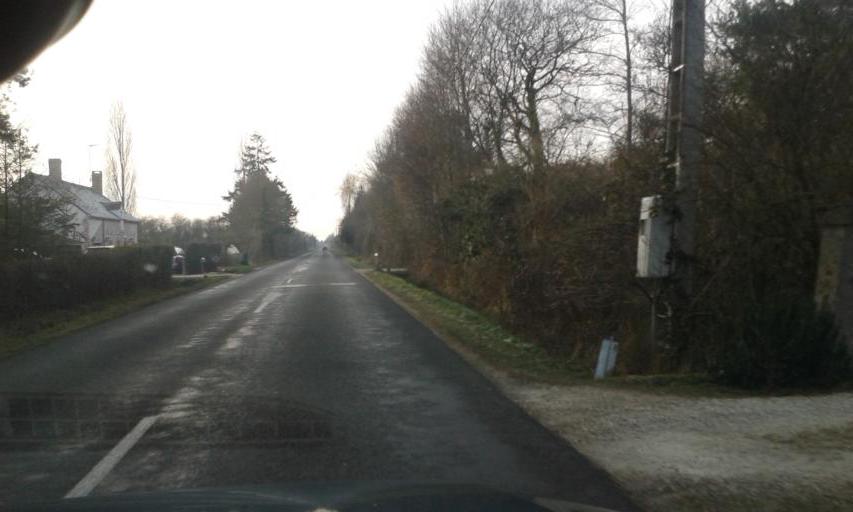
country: FR
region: Centre
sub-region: Departement du Loiret
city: Jouy-le-Potier
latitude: 47.7434
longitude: 1.8335
